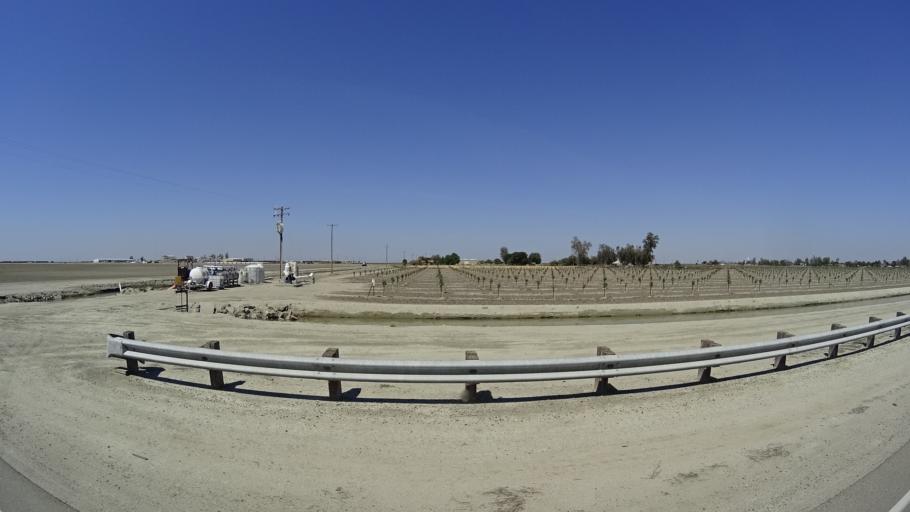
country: US
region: California
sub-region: Kings County
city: Corcoran
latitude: 36.0729
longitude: -119.5587
